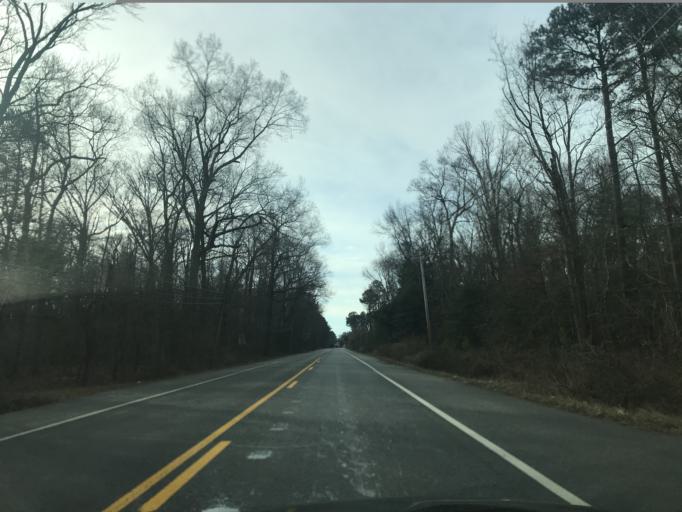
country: US
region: Maryland
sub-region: Charles County
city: Cobb Island
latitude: 38.2774
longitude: -76.8566
